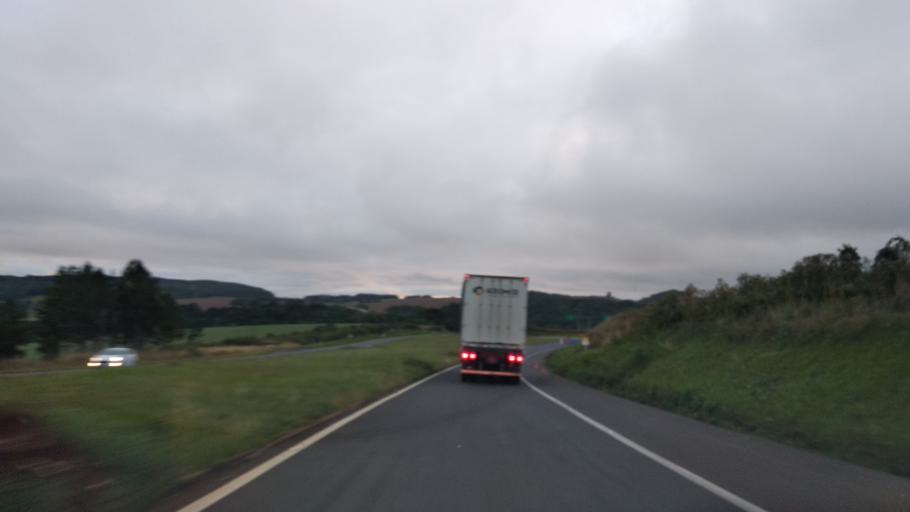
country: BR
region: Santa Catarina
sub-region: Campos Novos
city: Campos Novos
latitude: -27.3742
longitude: -51.0697
